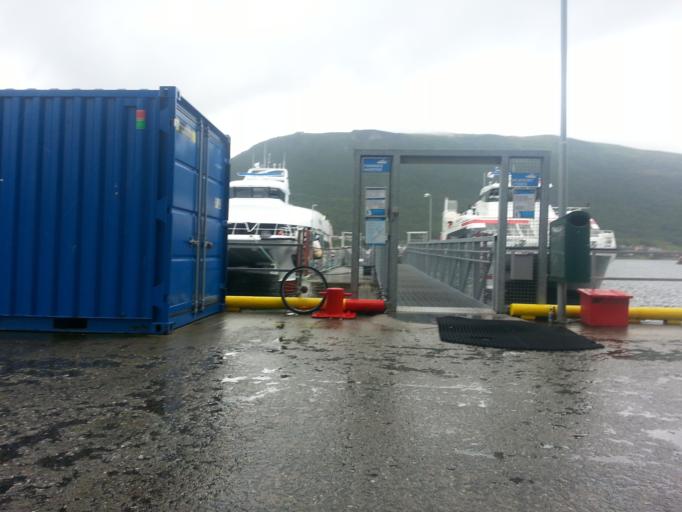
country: NO
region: Troms
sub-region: Tromso
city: Tromso
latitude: 69.6465
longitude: 18.9559
